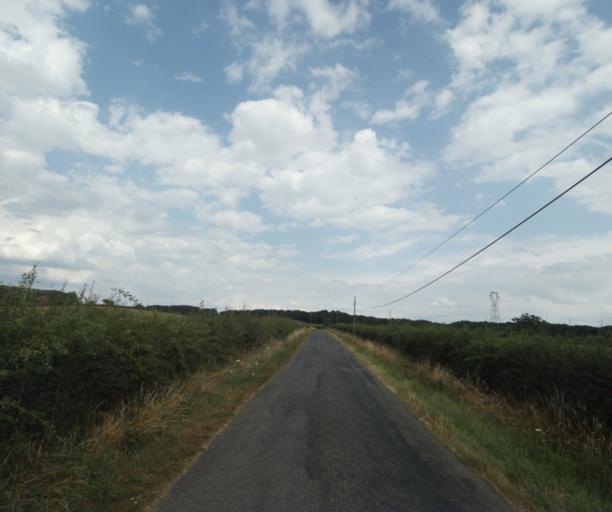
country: FR
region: Bourgogne
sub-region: Departement de Saone-et-Loire
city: Gueugnon
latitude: 46.6150
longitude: 4.0842
